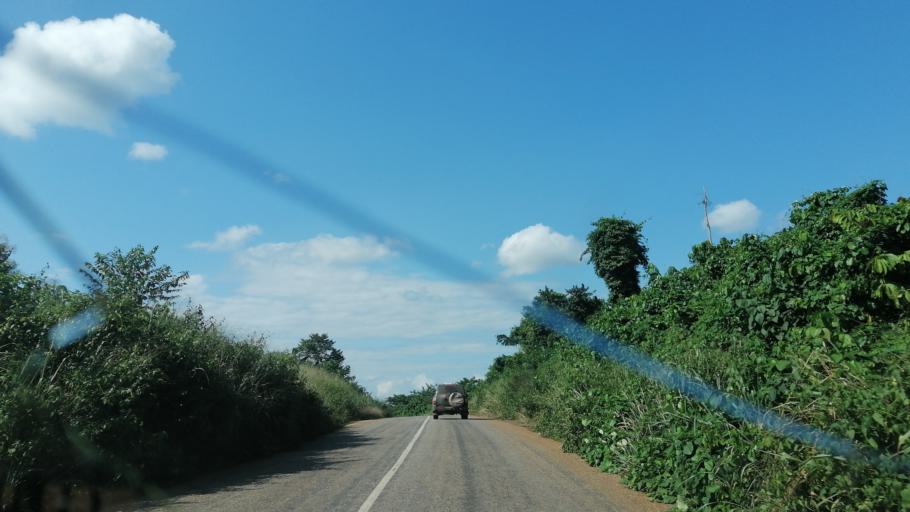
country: GH
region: Western
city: Bibiani
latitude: 6.7433
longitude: -2.5200
